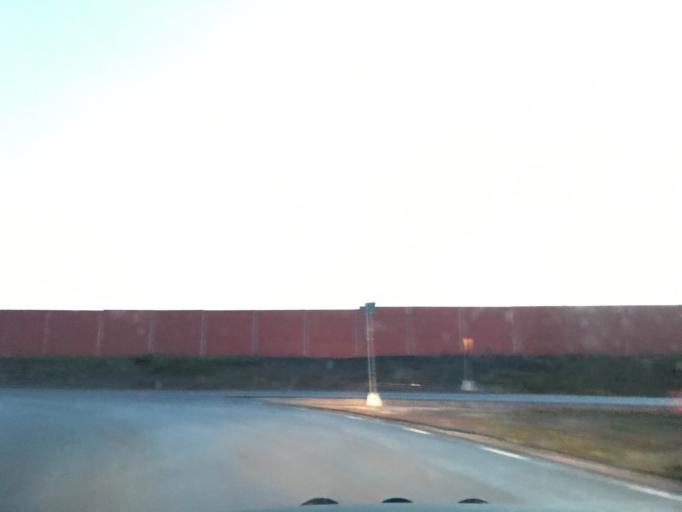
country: SE
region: Norrbotten
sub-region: Gallivare Kommun
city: Malmberget
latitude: 67.6524
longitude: 21.0164
